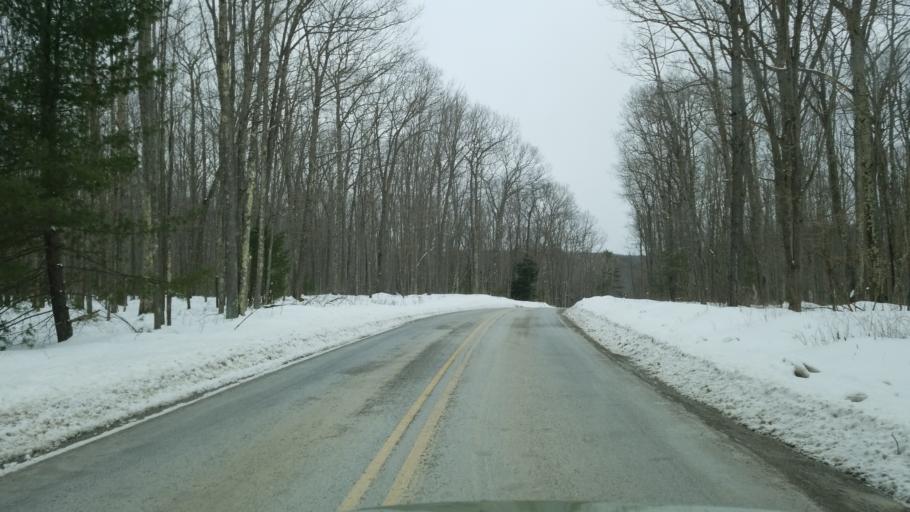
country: US
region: Pennsylvania
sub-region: Clearfield County
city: Shiloh
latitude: 41.2309
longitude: -78.1917
